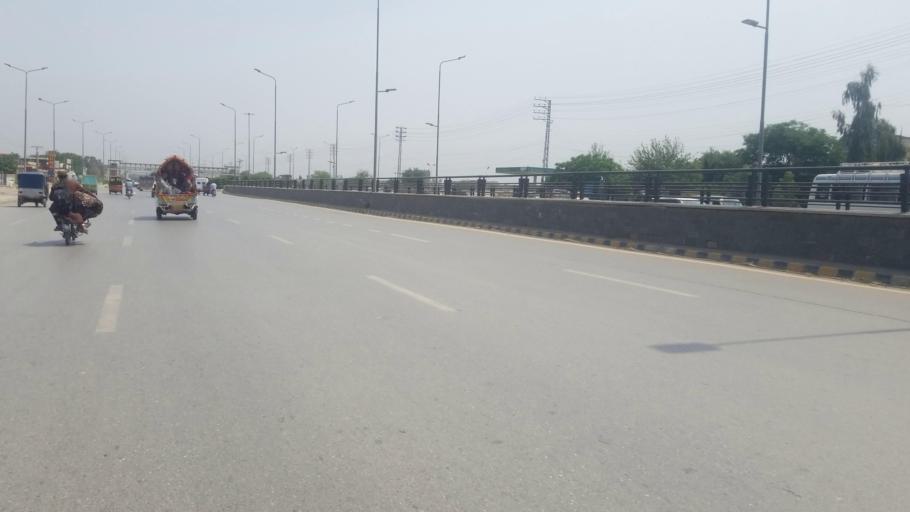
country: PK
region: Khyber Pakhtunkhwa
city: Peshawar
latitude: 34.0181
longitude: 71.6327
